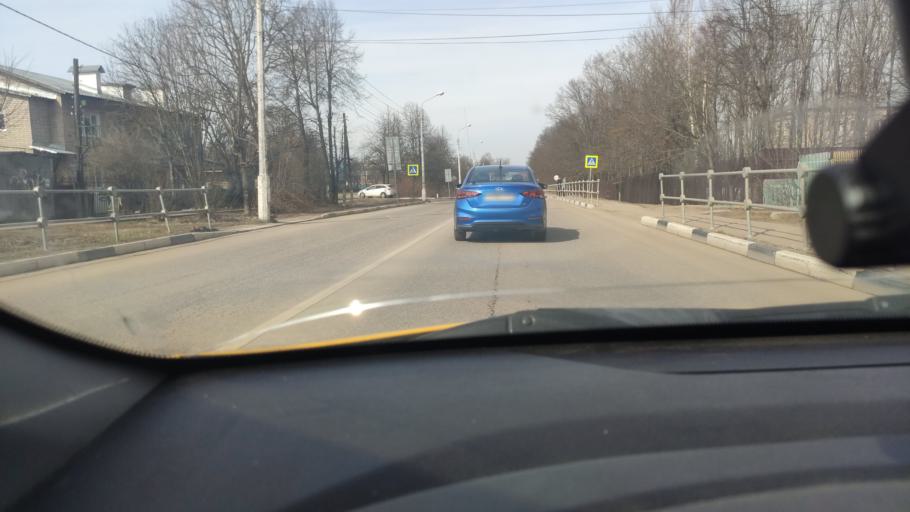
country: RU
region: Moskovskaya
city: Ruza
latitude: 55.7059
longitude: 36.1869
